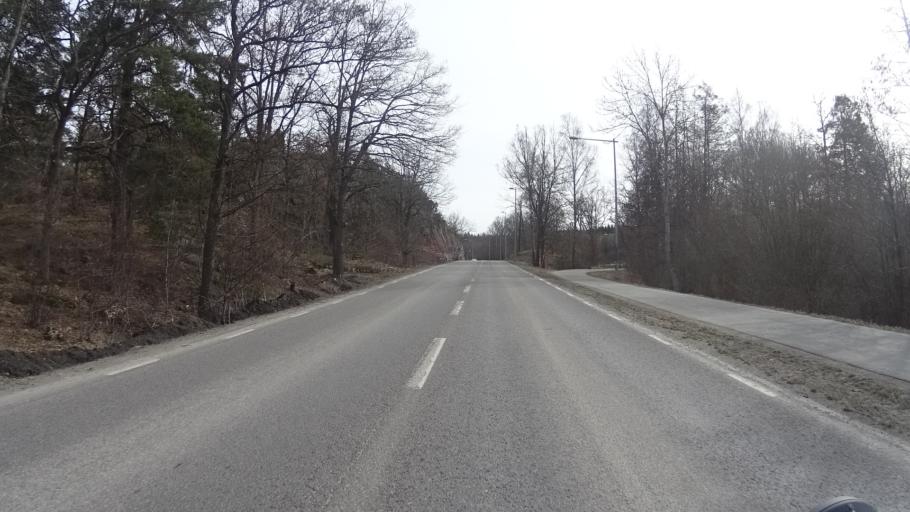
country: SE
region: Stockholm
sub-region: Nacka Kommun
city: Nacka
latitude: 59.2901
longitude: 18.1555
